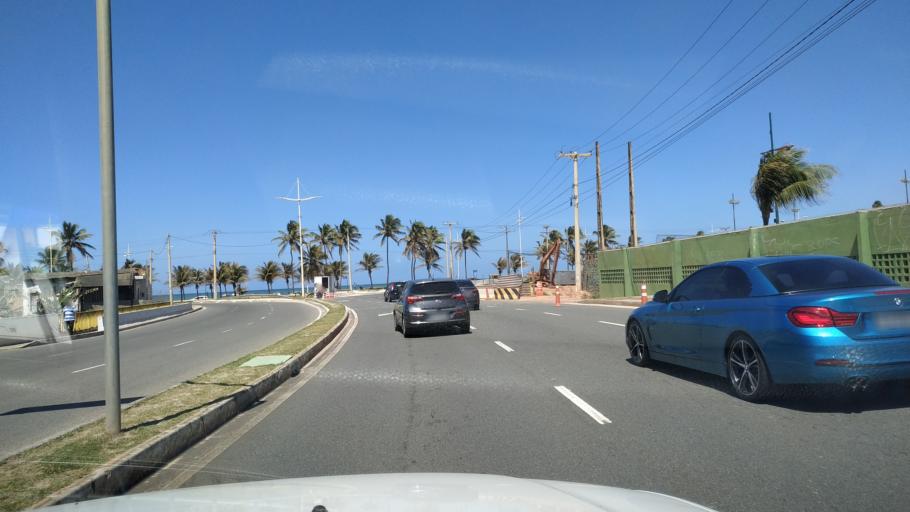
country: BR
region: Bahia
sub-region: Lauro De Freitas
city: Lauro de Freitas
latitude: -12.9536
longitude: -38.3851
